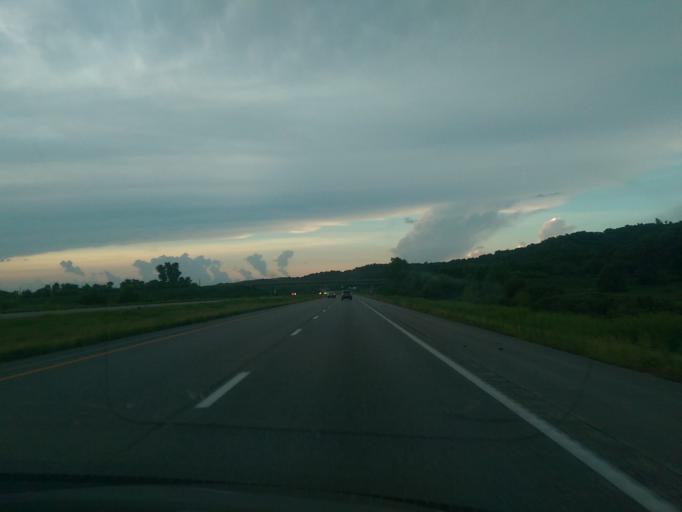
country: US
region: Missouri
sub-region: Atchison County
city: Rock Port
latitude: 40.3230
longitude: -95.4957
